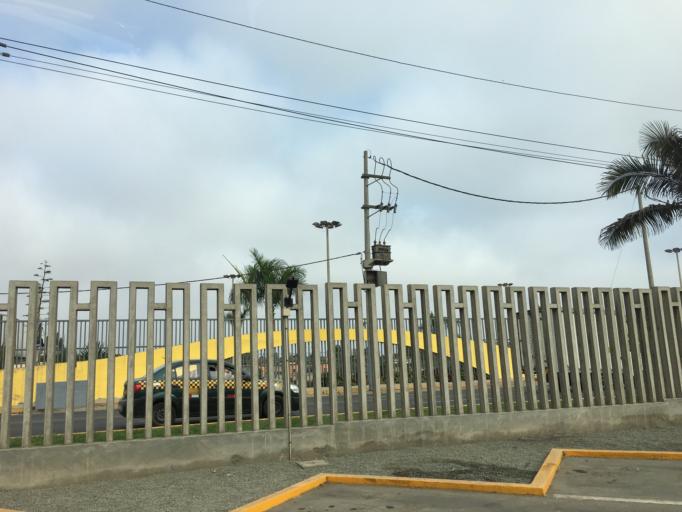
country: PE
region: Callao
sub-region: Callao
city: Callao
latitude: -12.0679
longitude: -77.0816
